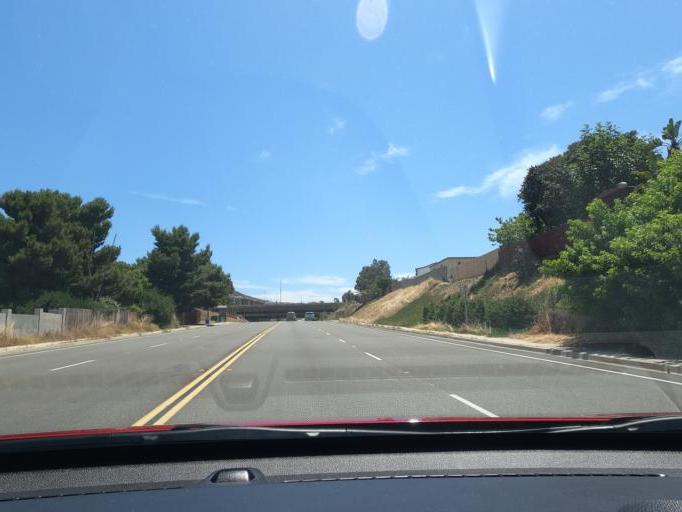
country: US
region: California
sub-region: San Diego County
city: Imperial Beach
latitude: 32.5736
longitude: -117.0415
